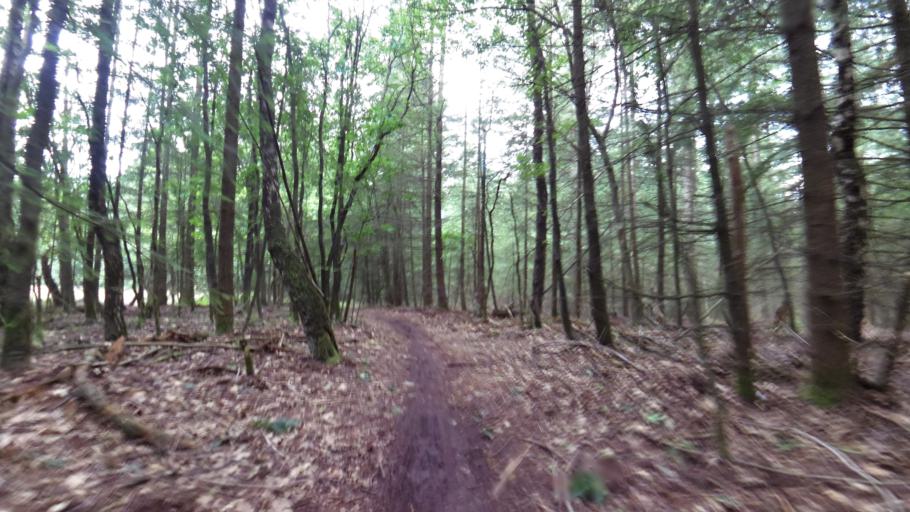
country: NL
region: Gelderland
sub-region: Gemeente Apeldoorn
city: Apeldoorn
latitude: 52.2108
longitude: 5.8964
